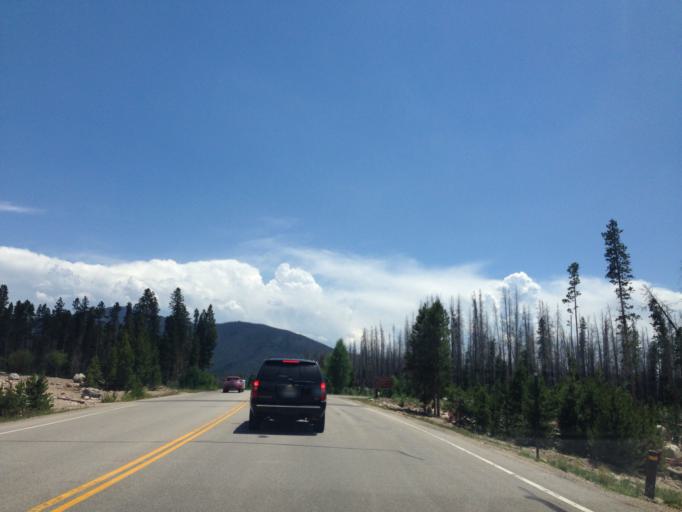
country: US
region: Colorado
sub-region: Grand County
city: Granby
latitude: 40.2676
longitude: -105.8340
